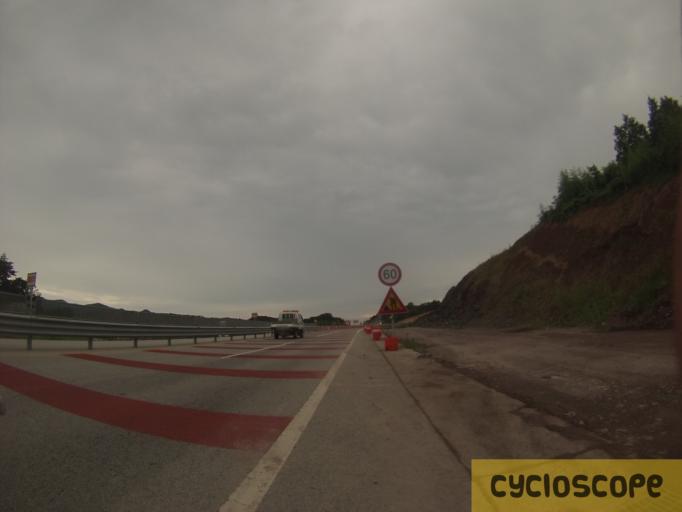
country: KR
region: Jeollabuk-do
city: Kimje
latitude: 35.7892
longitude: 126.8117
